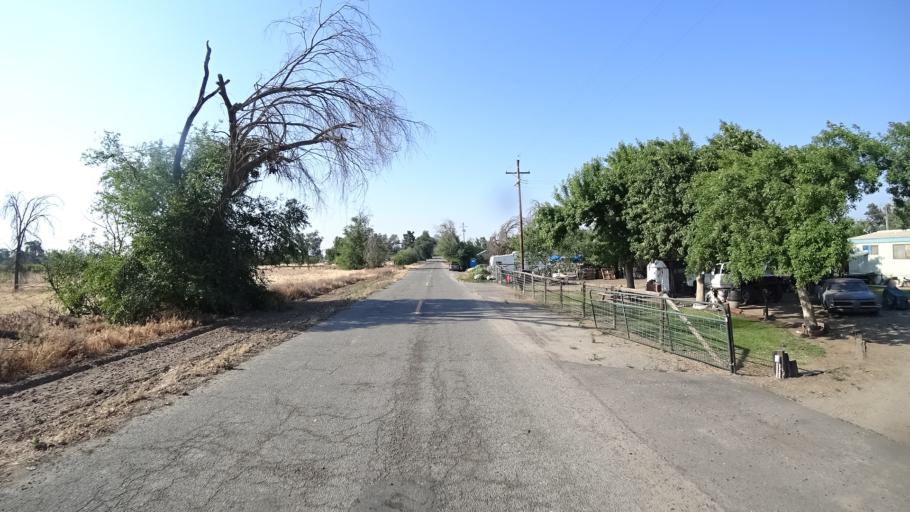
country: US
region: California
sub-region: Kings County
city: Lemoore
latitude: 36.3628
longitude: -119.8161
